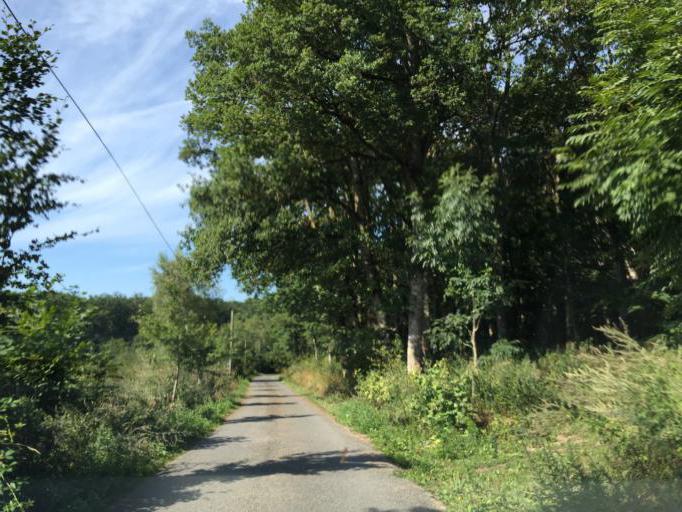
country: FR
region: Midi-Pyrenees
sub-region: Departement de l'Aveyron
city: Pont-de-Salars
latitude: 44.3048
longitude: 2.7188
